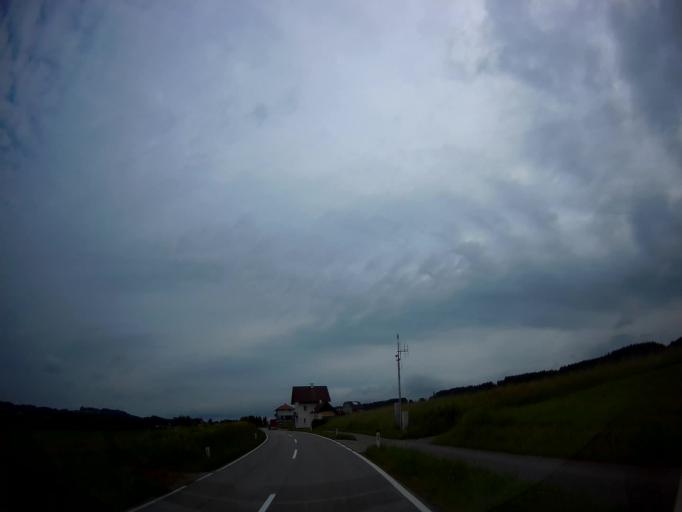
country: AT
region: Salzburg
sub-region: Politischer Bezirk Salzburg-Umgebung
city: Mattsee
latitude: 48.0032
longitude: 13.1232
